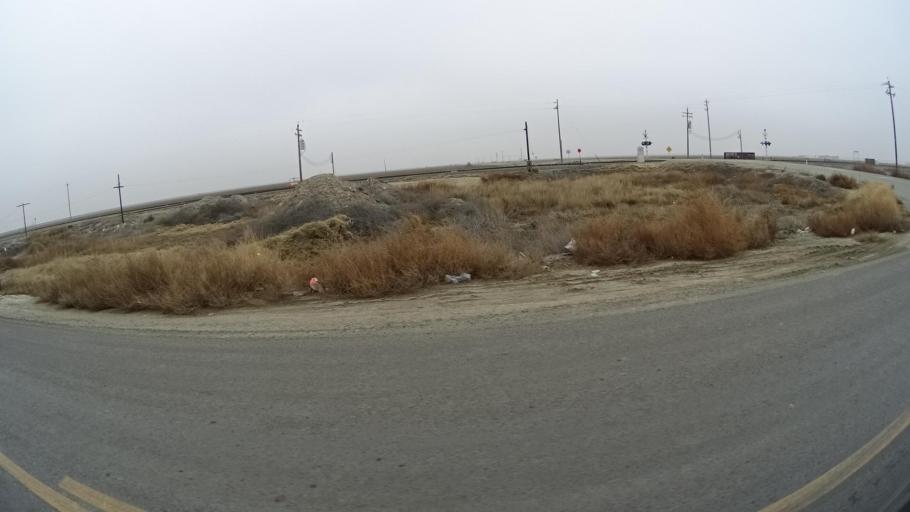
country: US
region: California
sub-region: Kern County
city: Rosedale
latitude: 35.1804
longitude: -119.1987
